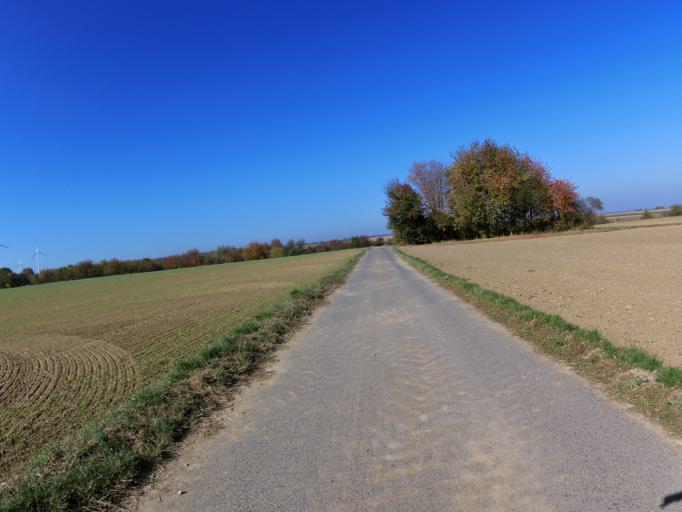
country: DE
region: Bavaria
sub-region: Regierungsbezirk Unterfranken
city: Geroldshausen
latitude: 49.6921
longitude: 9.9106
